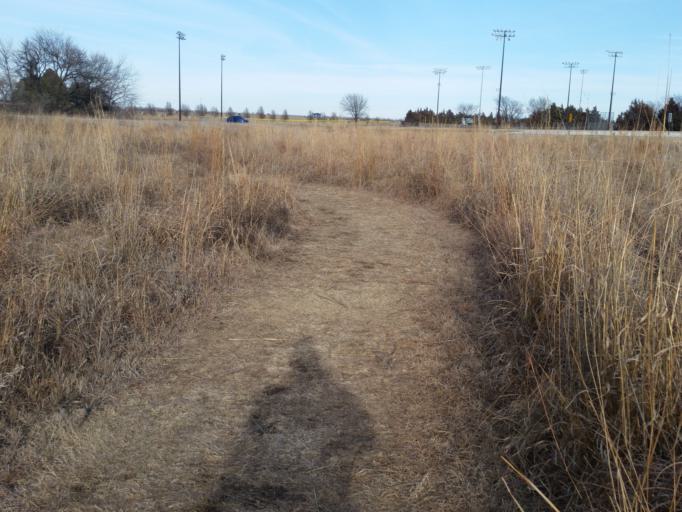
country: US
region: Kansas
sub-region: Harvey County
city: North Newton
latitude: 38.0624
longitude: -97.3376
